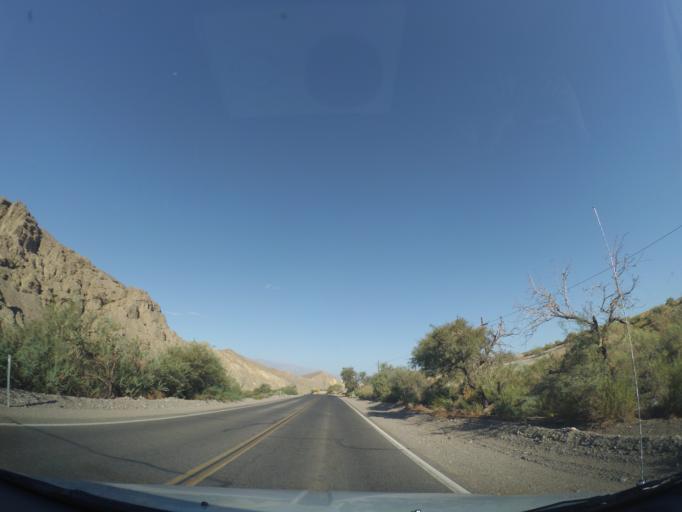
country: US
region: Nevada
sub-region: Nye County
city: Beatty
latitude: 36.4410
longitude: -116.8331
